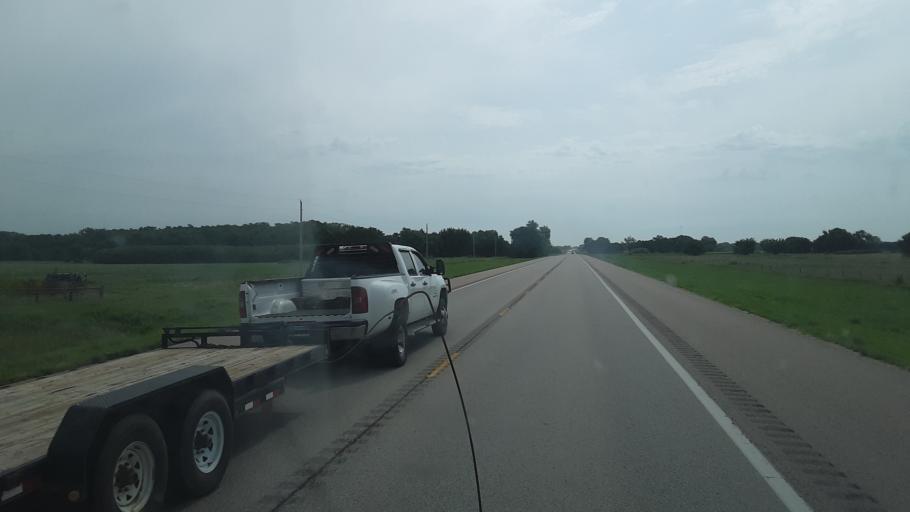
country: US
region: Kansas
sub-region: Stafford County
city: Stafford
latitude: 37.9842
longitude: -98.3493
